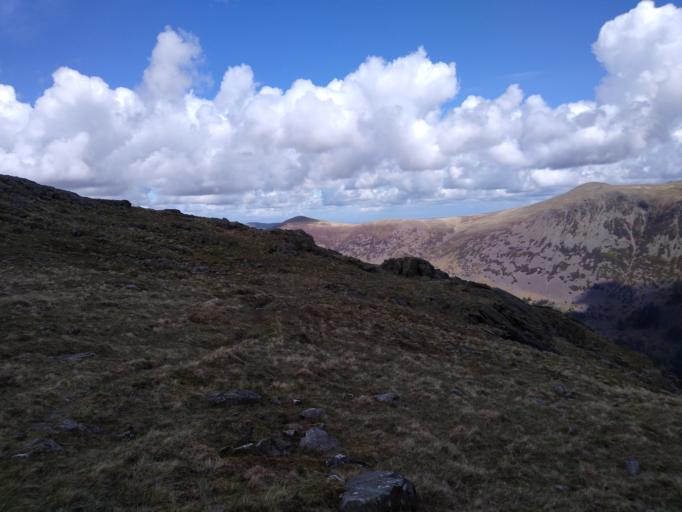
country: GB
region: England
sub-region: Cumbria
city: Cockermouth
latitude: 54.4982
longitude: -3.3066
